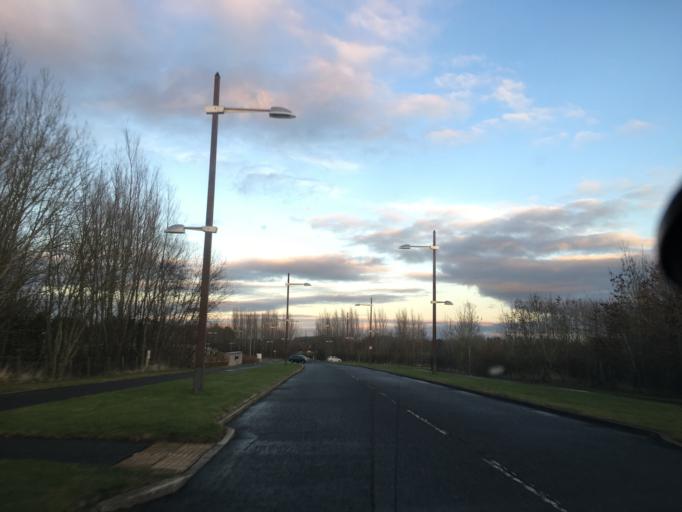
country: GB
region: Scotland
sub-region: Midlothian
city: Loanhead
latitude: 55.8604
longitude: -3.1899
